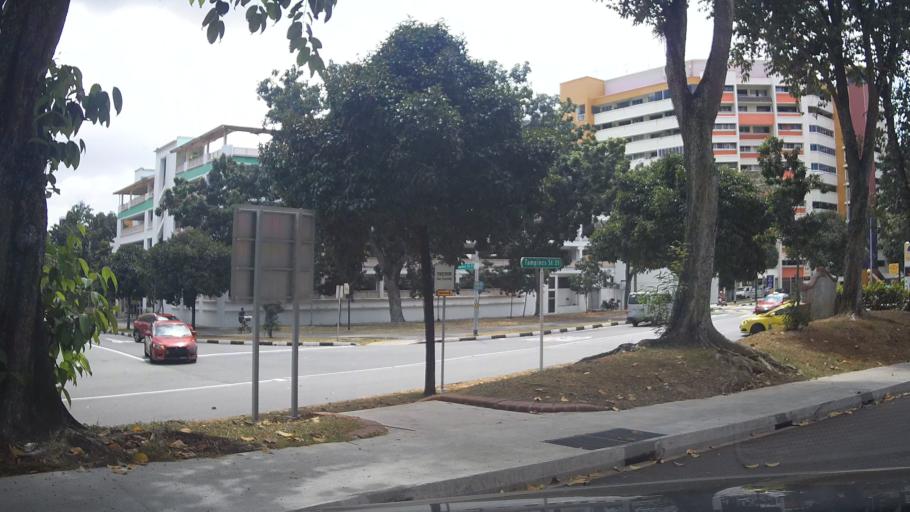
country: SG
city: Singapore
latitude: 1.3541
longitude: 103.9514
